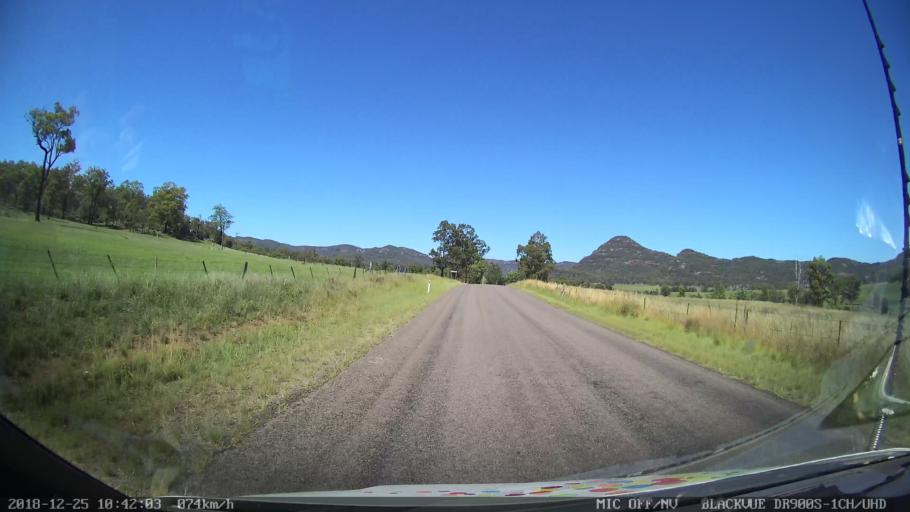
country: AU
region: New South Wales
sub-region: Upper Hunter Shire
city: Merriwa
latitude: -32.4142
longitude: 150.3282
